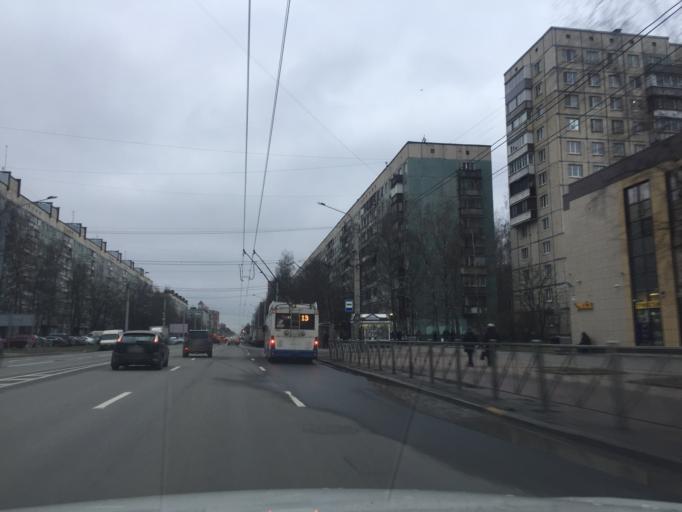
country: RU
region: Leningrad
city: Akademicheskoe
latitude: 60.0252
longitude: 30.3832
